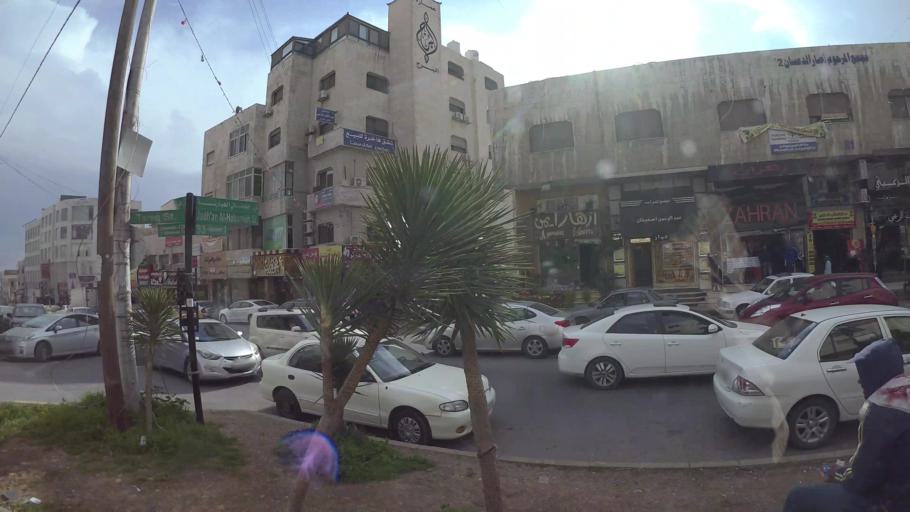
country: JO
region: Amman
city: Amman
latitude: 31.9994
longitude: 35.9447
